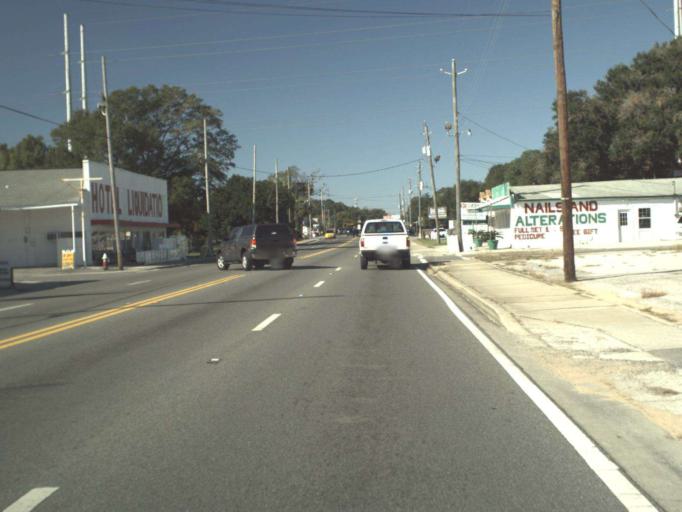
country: US
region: Florida
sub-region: Escambia County
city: West Pensacola
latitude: 30.4227
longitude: -87.2563
